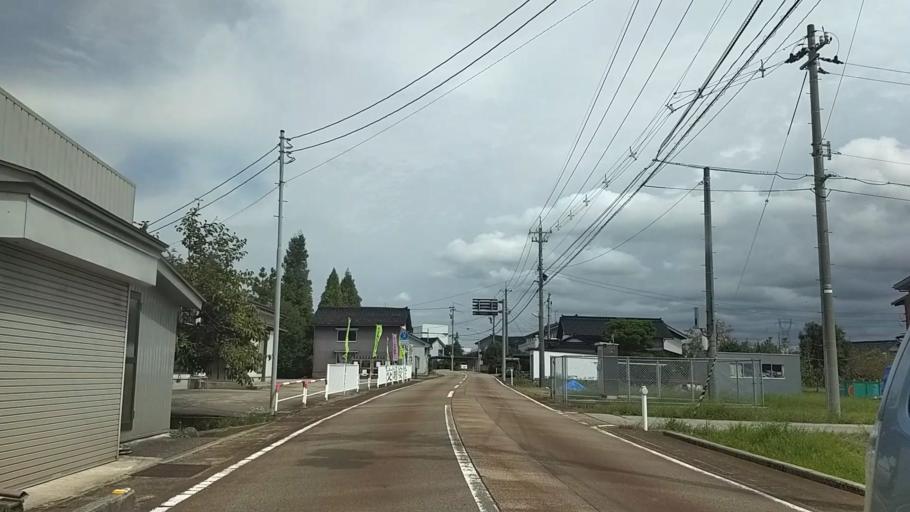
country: JP
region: Toyama
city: Kamiichi
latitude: 36.7402
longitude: 137.3727
